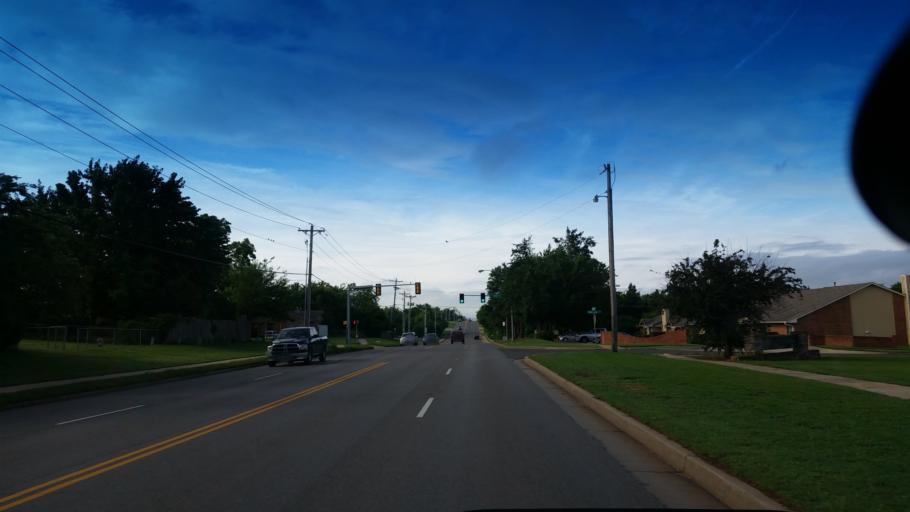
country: US
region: Oklahoma
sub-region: Oklahoma County
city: Edmond
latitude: 35.6615
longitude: -97.4961
